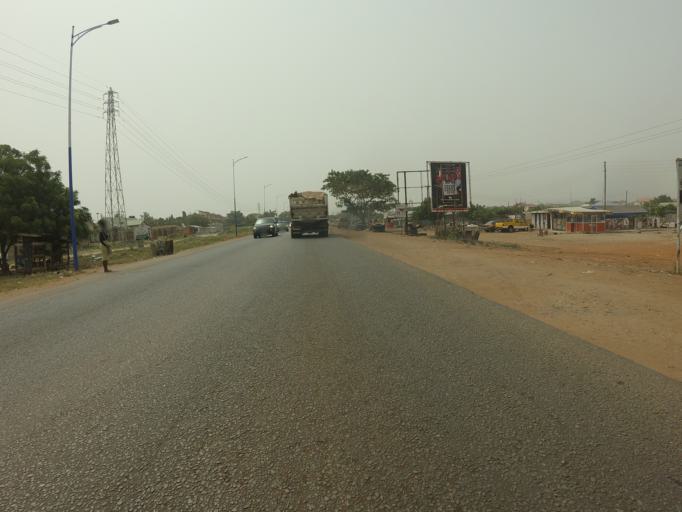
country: GH
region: Greater Accra
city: Tema
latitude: 5.7535
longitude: 0.0457
